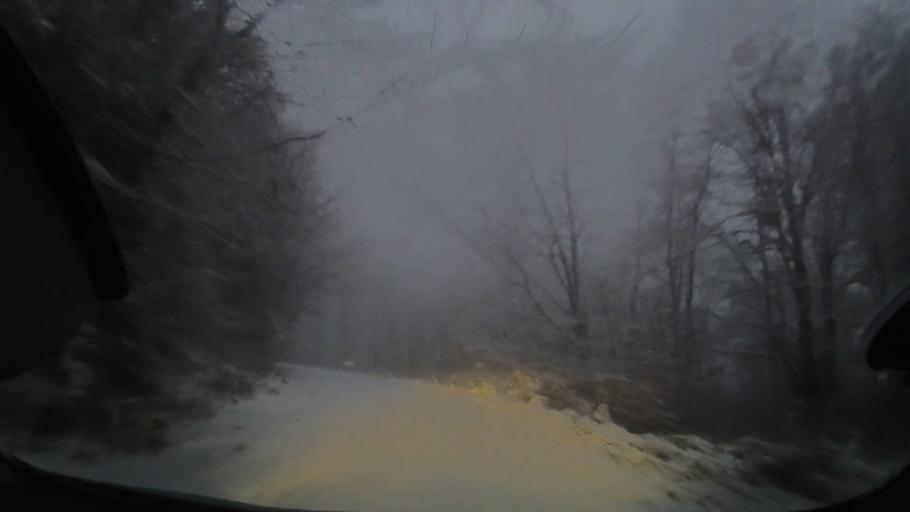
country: RO
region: Alba
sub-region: Comuna Avram Iancu
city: Avram Iancu
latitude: 46.3102
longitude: 22.8120
